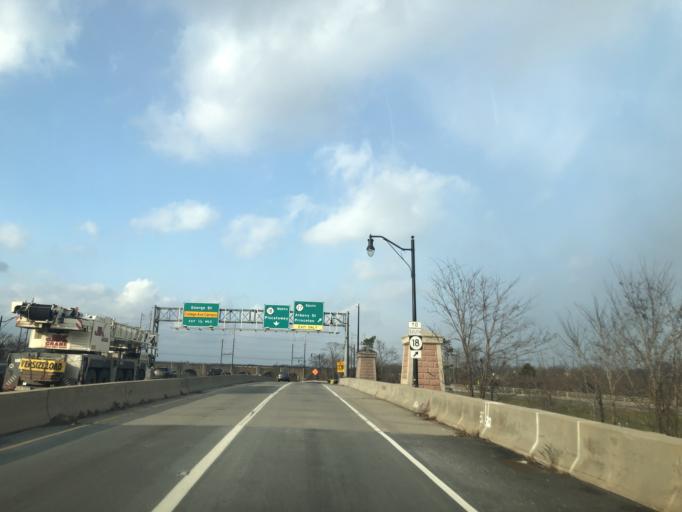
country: US
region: New Jersey
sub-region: Middlesex County
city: Highland Park
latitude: 40.4966
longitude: -74.4394
